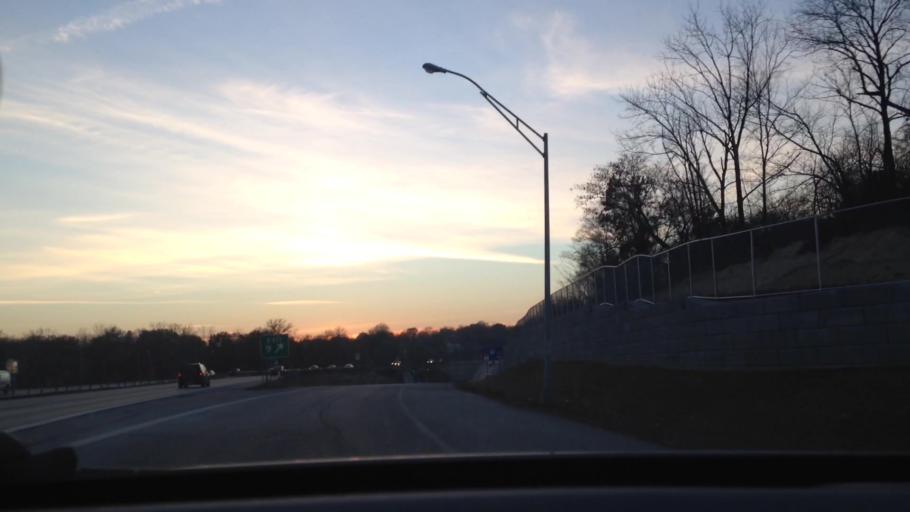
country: US
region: Missouri
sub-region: Clay County
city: Gladstone
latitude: 39.1753
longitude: -94.5345
